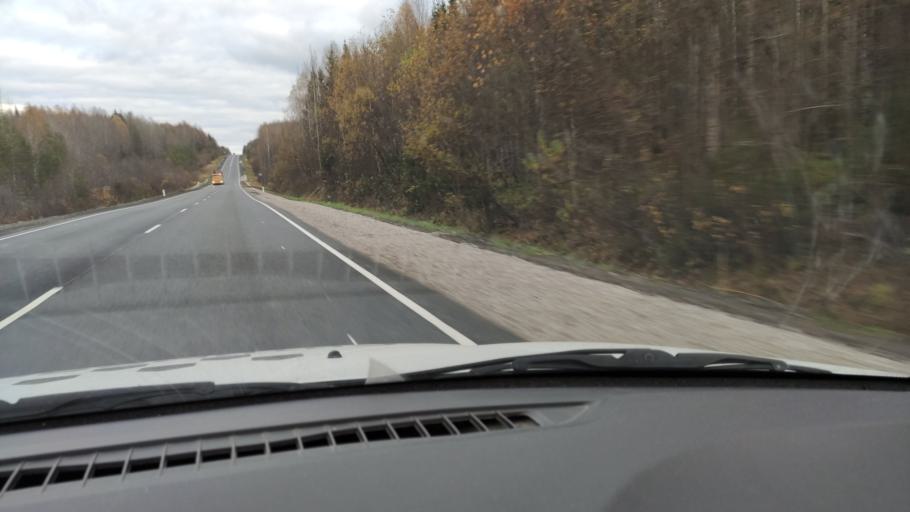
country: RU
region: Kirov
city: Chernaya Kholunitsa
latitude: 58.8894
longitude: 51.3625
